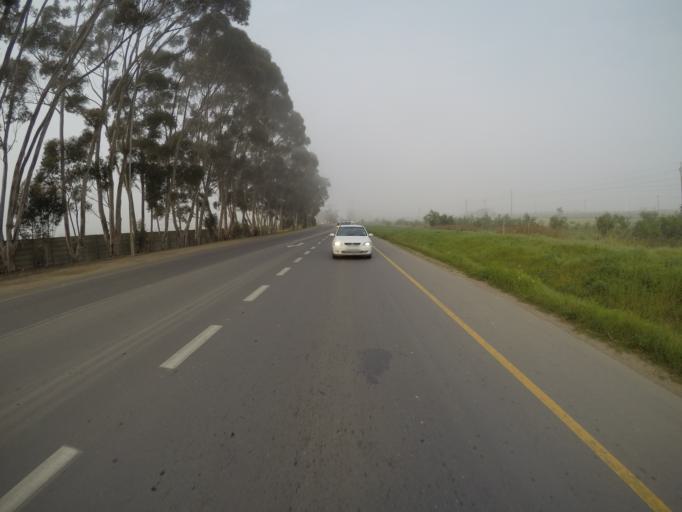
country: ZA
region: Western Cape
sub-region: City of Cape Town
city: Kraaifontein
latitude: -33.7903
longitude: 18.6981
